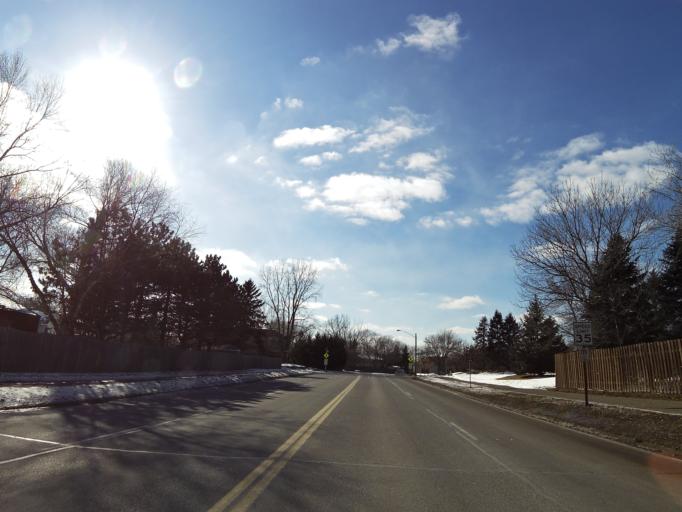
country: US
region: Minnesota
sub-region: Washington County
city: Woodbury
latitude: 44.9051
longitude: -92.9568
